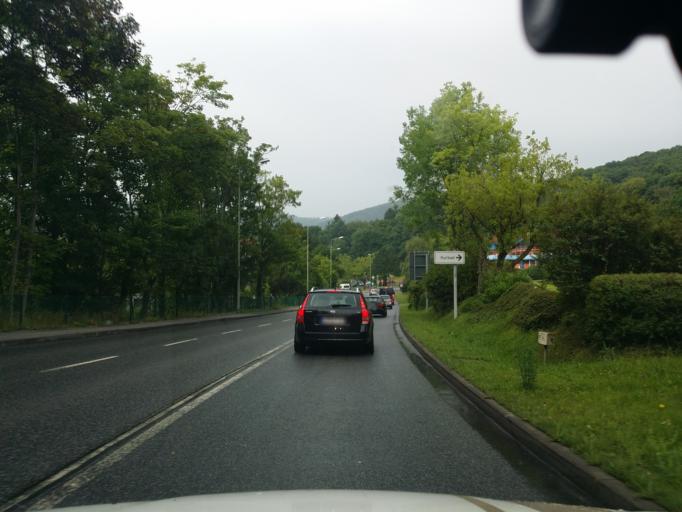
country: DE
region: Hesse
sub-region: Regierungsbezirk Darmstadt
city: Konigstein im Taunus
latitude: 50.1847
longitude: 8.4691
